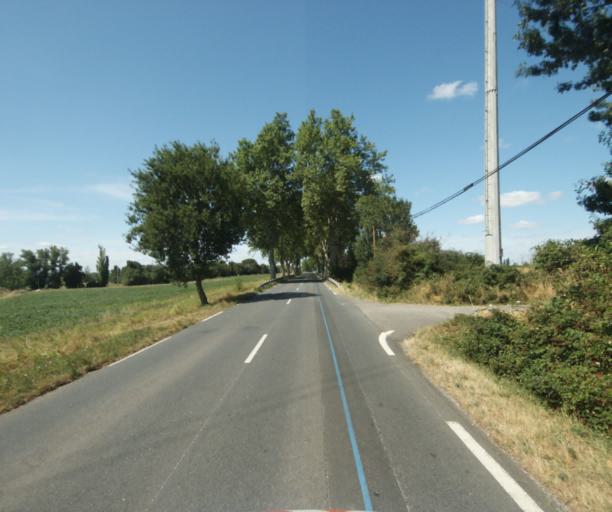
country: FR
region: Midi-Pyrenees
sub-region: Departement de la Haute-Garonne
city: Revel
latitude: 43.4830
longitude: 2.0142
